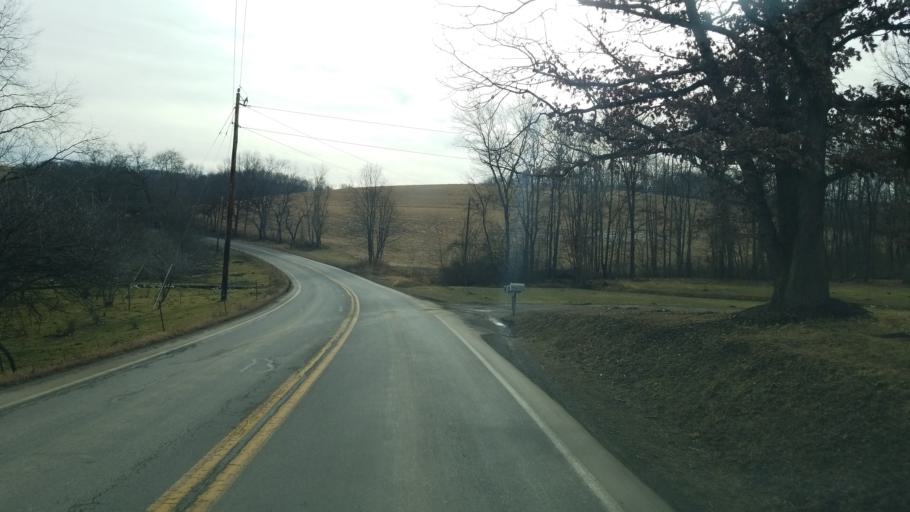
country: US
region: Pennsylvania
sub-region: Jefferson County
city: Punxsutawney
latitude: 40.8938
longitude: -79.0425
